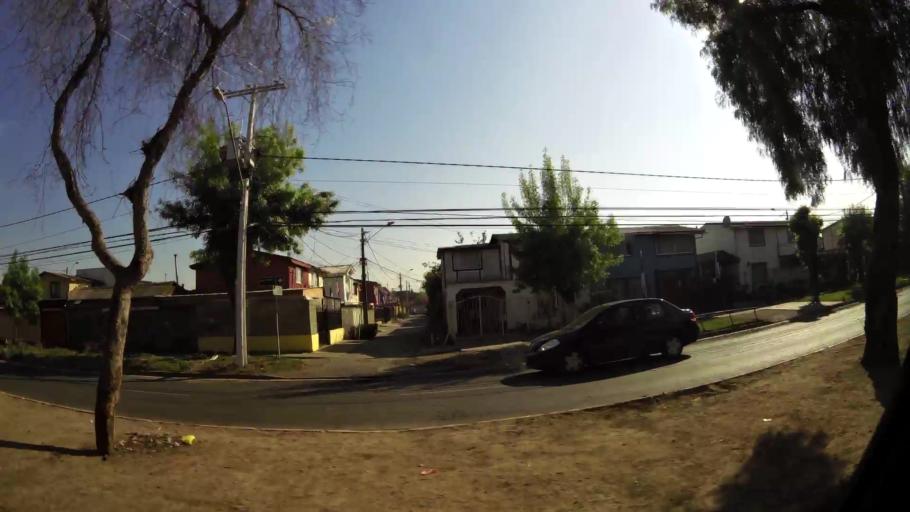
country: CL
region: Santiago Metropolitan
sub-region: Provincia de Santiago
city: Lo Prado
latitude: -33.4547
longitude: -70.7571
